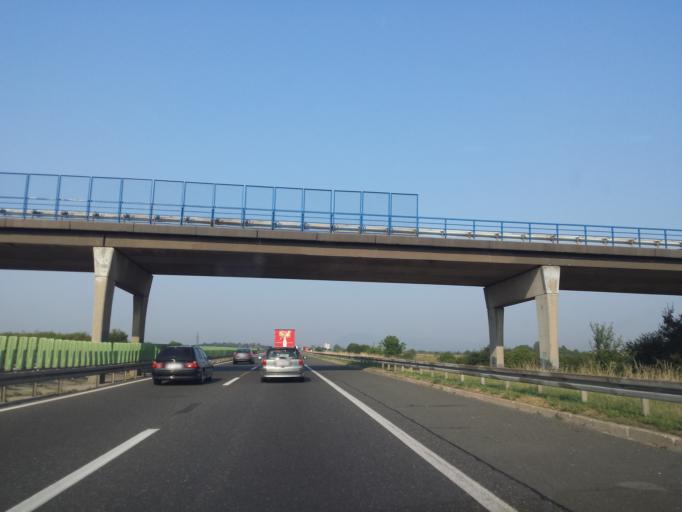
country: HR
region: Grad Zagreb
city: Zadvorsko
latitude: 45.7488
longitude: 15.9355
